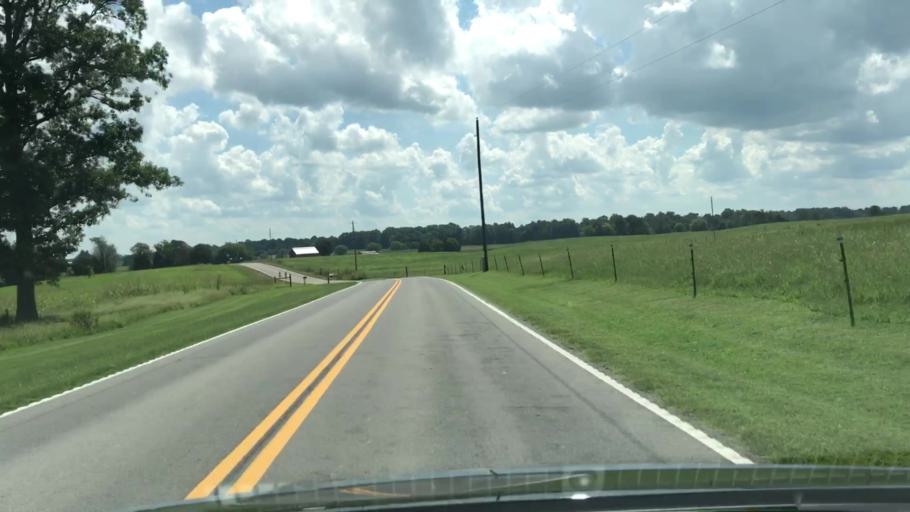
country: US
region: Tennessee
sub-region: Robertson County
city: Springfield
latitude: 36.5894
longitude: -86.8963
